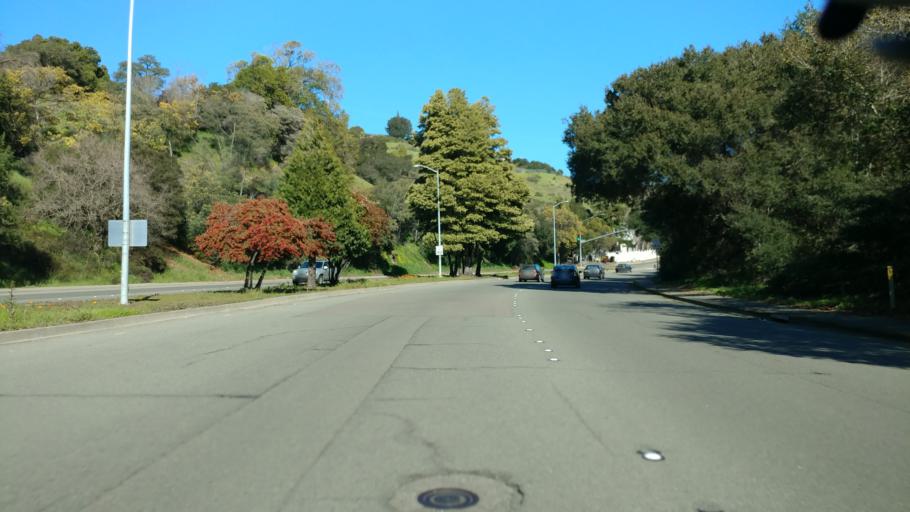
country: US
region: California
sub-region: Alameda County
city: Fairview
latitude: 37.7027
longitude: -122.0523
